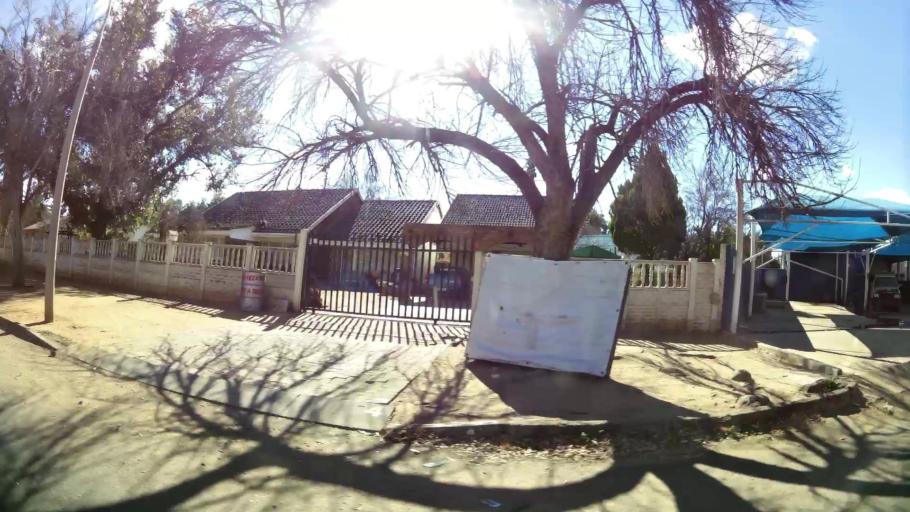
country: ZA
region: North-West
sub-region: Dr Kenneth Kaunda District Municipality
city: Klerksdorp
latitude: -26.8623
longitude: 26.6369
